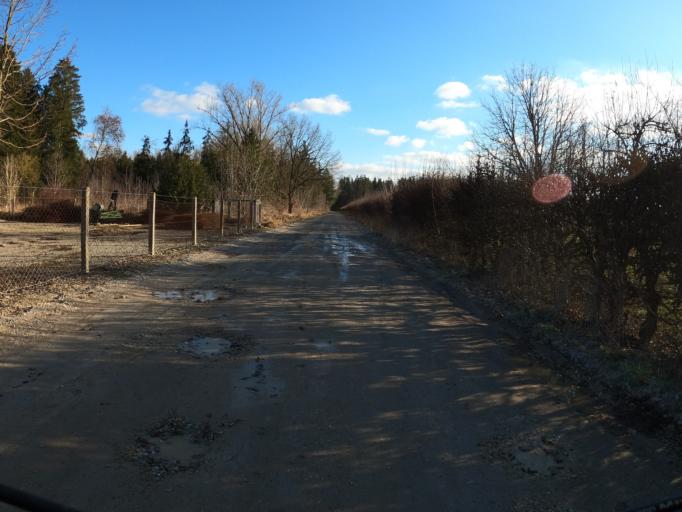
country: DE
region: Bavaria
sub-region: Swabia
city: Leipheim
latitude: 48.4286
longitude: 10.2270
